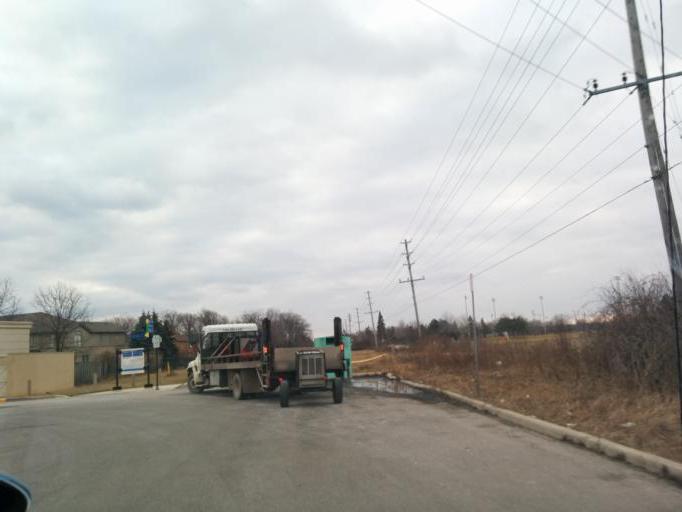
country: CA
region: Ontario
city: Burlington
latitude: 43.3891
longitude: -79.7488
